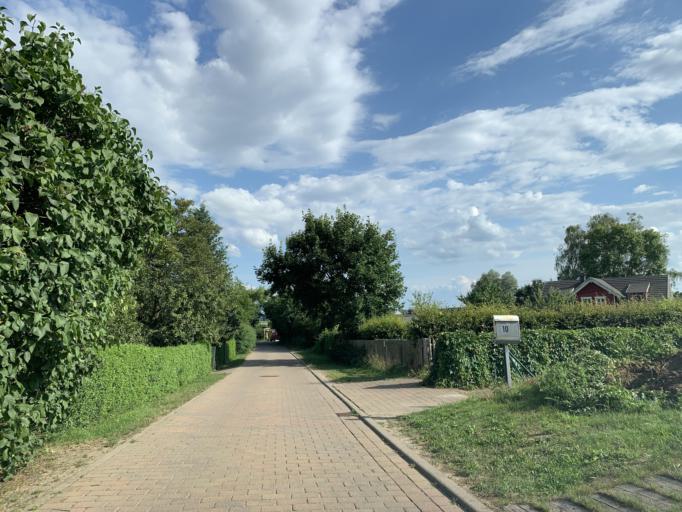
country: DE
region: Mecklenburg-Vorpommern
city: Blankensee
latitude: 53.3941
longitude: 13.2330
